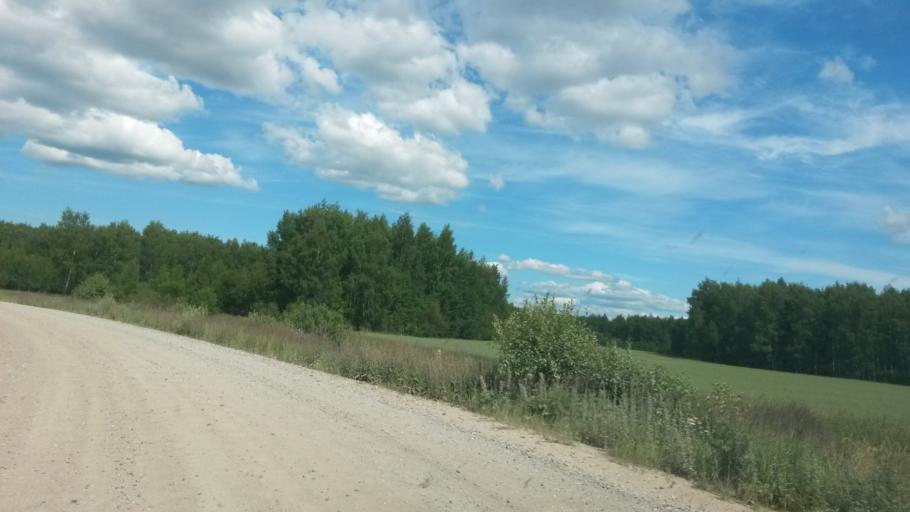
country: RU
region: Ivanovo
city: Zavolzhsk
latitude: 57.4652
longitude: 42.2094
